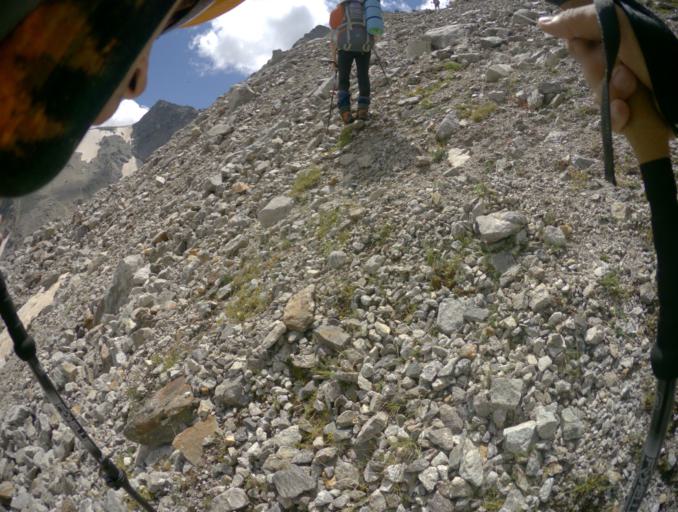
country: RU
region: Karachayevo-Cherkesiya
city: Uchkulan
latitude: 43.3212
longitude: 42.0815
